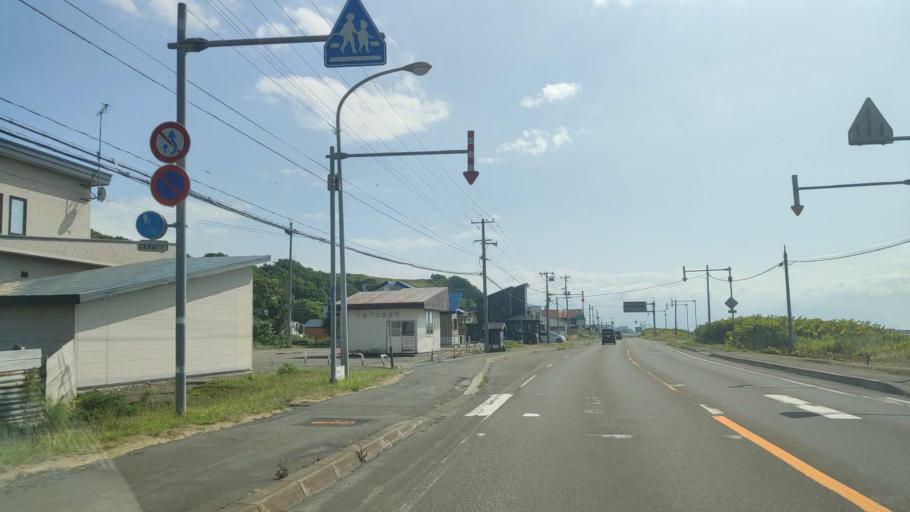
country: JP
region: Hokkaido
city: Rumoi
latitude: 43.9656
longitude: 141.6455
